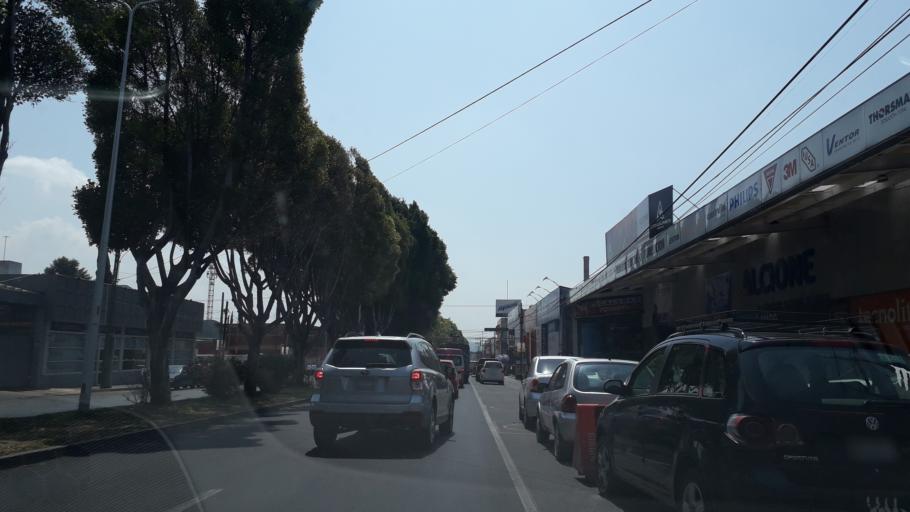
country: MX
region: Puebla
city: Puebla
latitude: 19.0539
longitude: -98.2133
